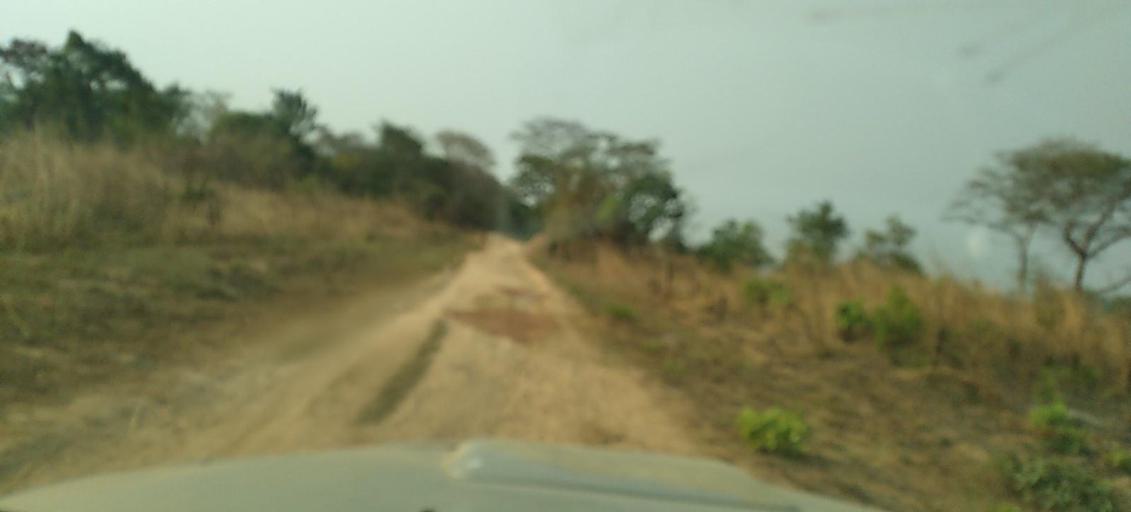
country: ZM
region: North-Western
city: Kasempa
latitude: -13.2821
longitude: 26.5549
